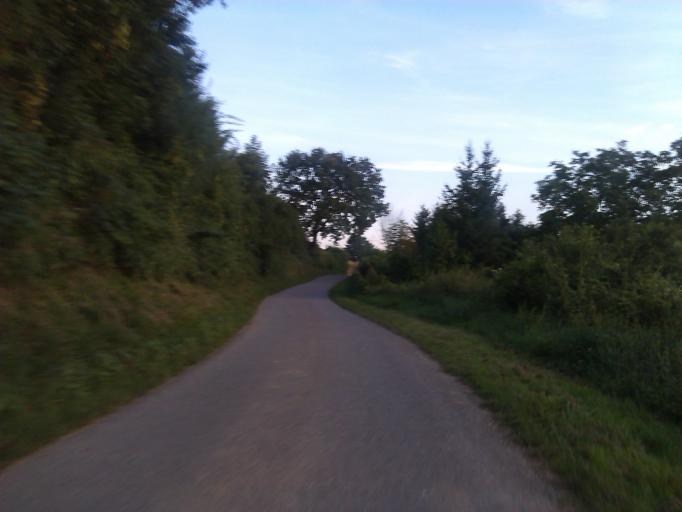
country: DE
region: Baden-Wuerttemberg
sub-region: Karlsruhe Region
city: Sinsheim
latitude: 49.1942
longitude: 8.8691
